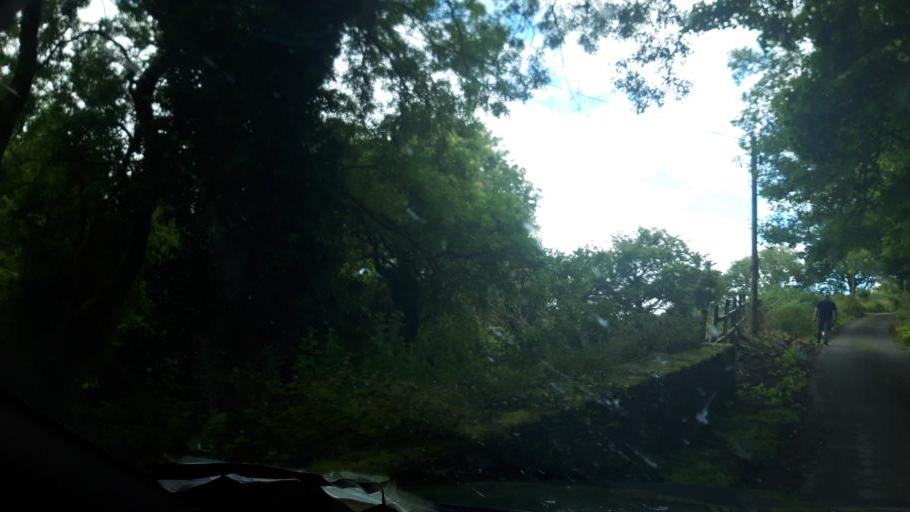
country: IE
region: Munster
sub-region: South Tipperary
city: Cluain Meala
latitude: 52.3454
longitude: -7.6941
